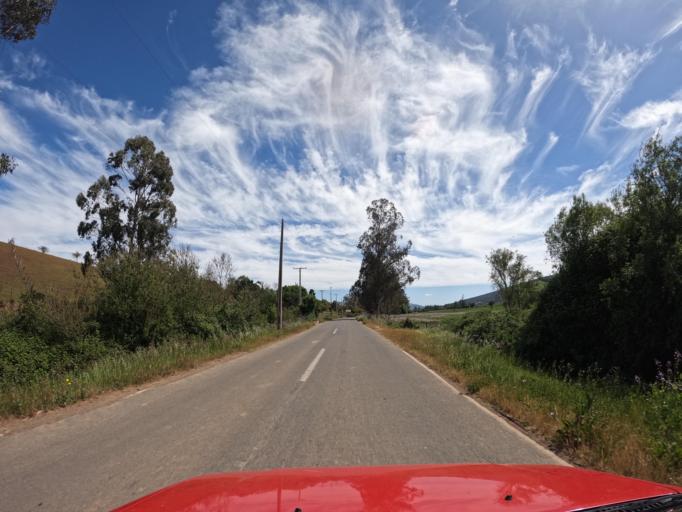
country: CL
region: Maule
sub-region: Provincia de Talca
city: Constitucion
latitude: -35.0046
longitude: -72.0286
